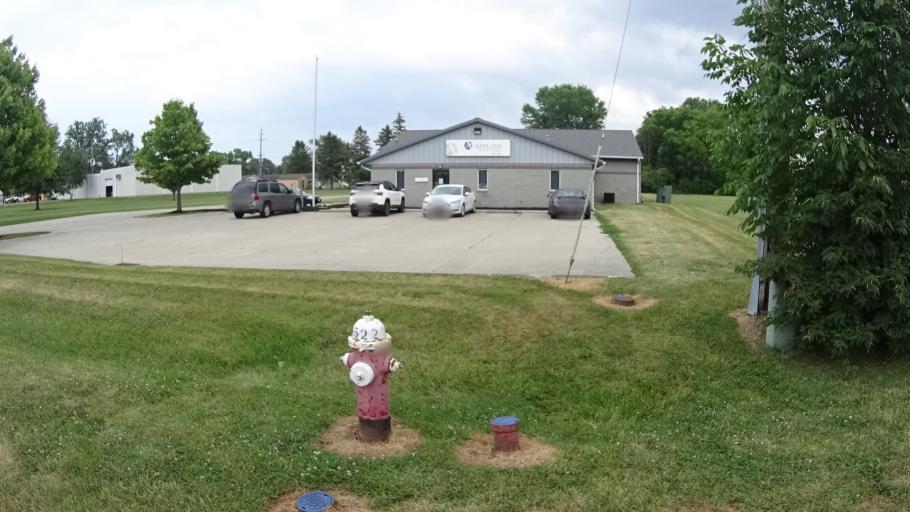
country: US
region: Ohio
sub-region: Erie County
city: Sandusky
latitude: 41.4397
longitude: -82.7434
